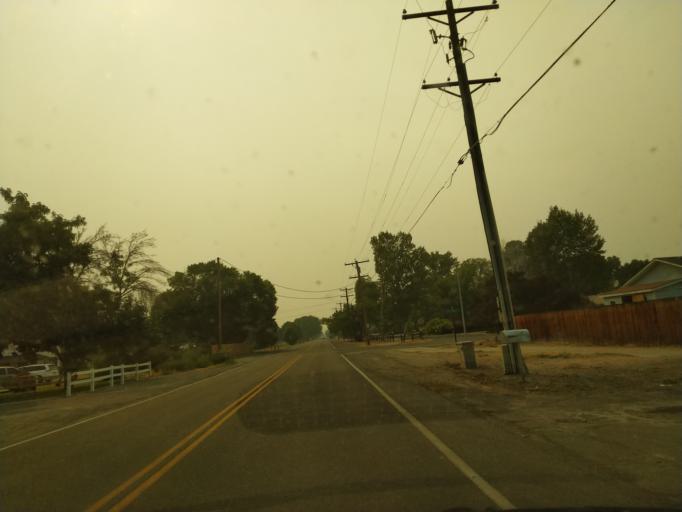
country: US
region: Colorado
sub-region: Mesa County
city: Fruitvale
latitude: 39.0846
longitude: -108.4825
